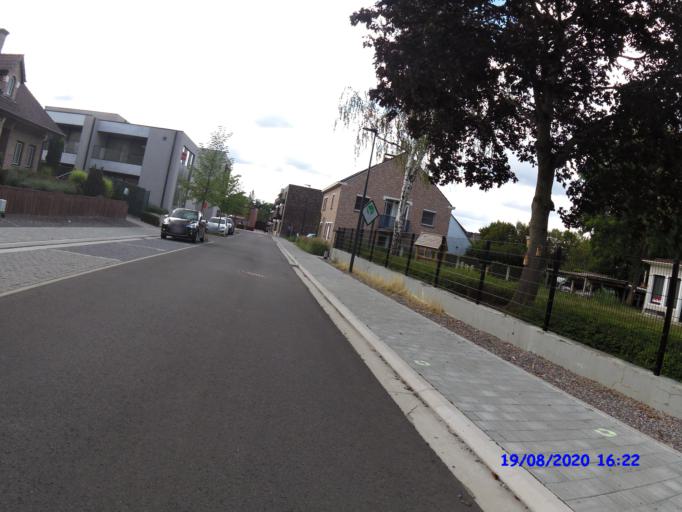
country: BE
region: Flanders
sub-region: Provincie Limburg
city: Nieuwerkerken
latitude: 50.8651
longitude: 5.1958
